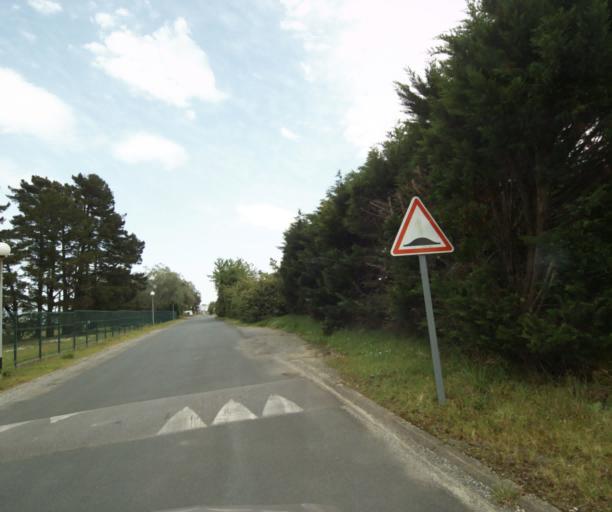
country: FR
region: Aquitaine
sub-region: Departement des Pyrenees-Atlantiques
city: Mouguerre
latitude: 43.4855
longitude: -1.4334
